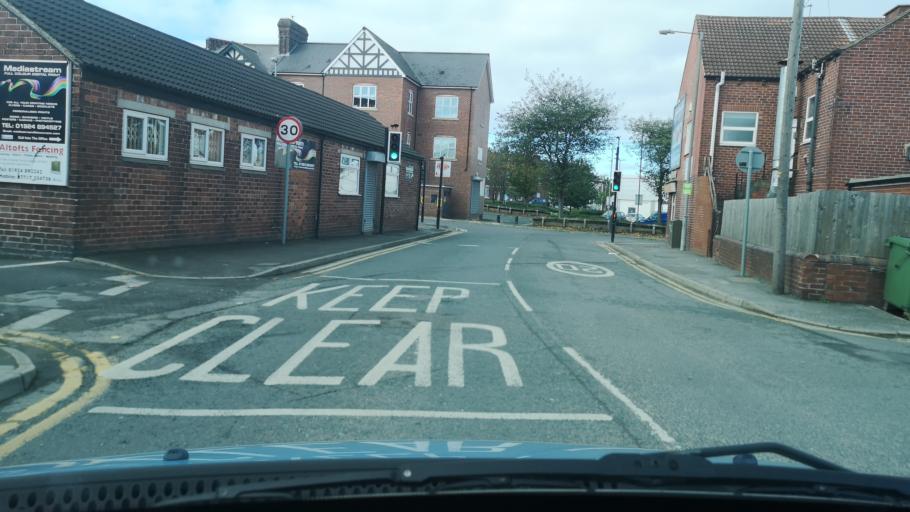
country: GB
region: England
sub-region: City and Borough of Wakefield
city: Normanton
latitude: 53.7005
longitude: -1.4199
